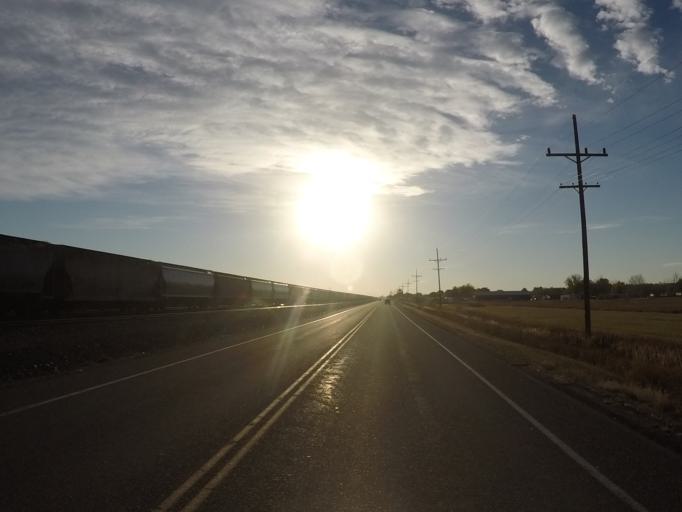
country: US
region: Montana
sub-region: Yellowstone County
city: Laurel
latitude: 45.6803
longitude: -108.7252
